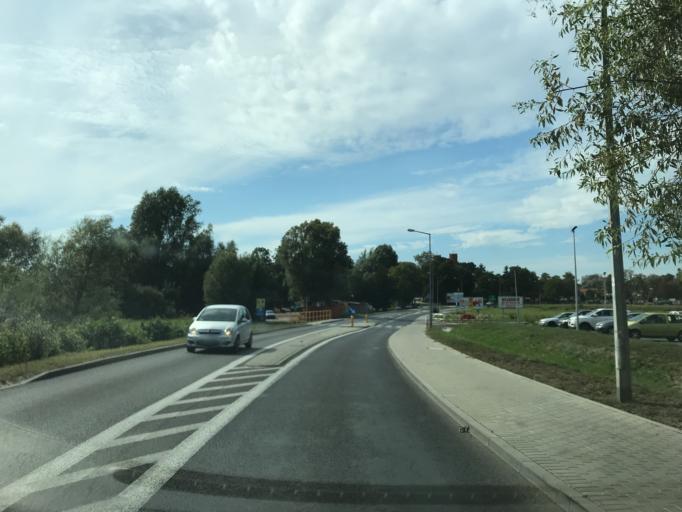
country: PL
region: Pomeranian Voivodeship
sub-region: Powiat pucki
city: Krokowa
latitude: 54.7803
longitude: 18.1682
